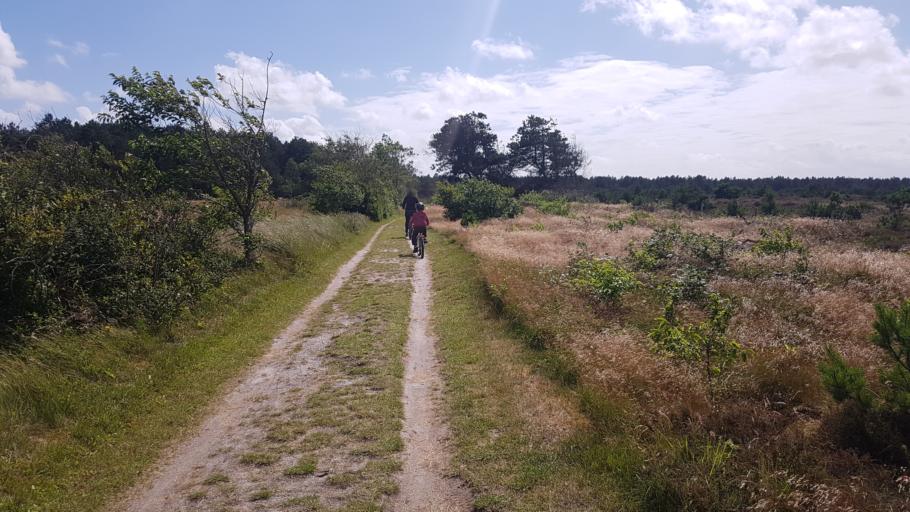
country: DE
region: Schleswig-Holstein
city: List
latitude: 55.1268
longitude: 8.5392
